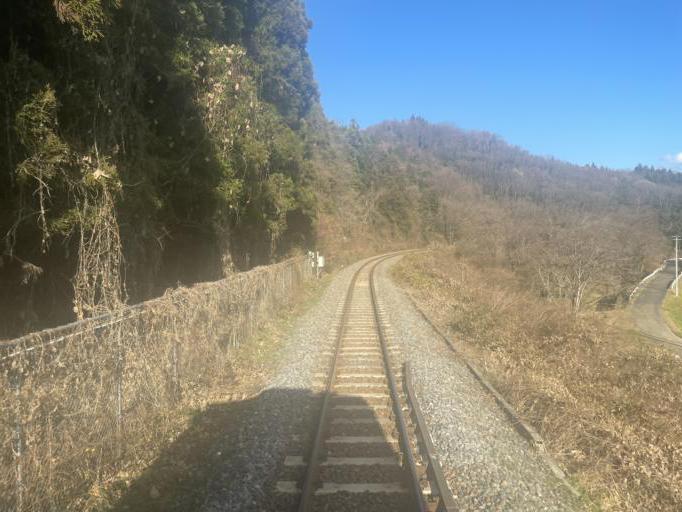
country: JP
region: Iwate
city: Ichinoseki
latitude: 38.9131
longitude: 141.2277
